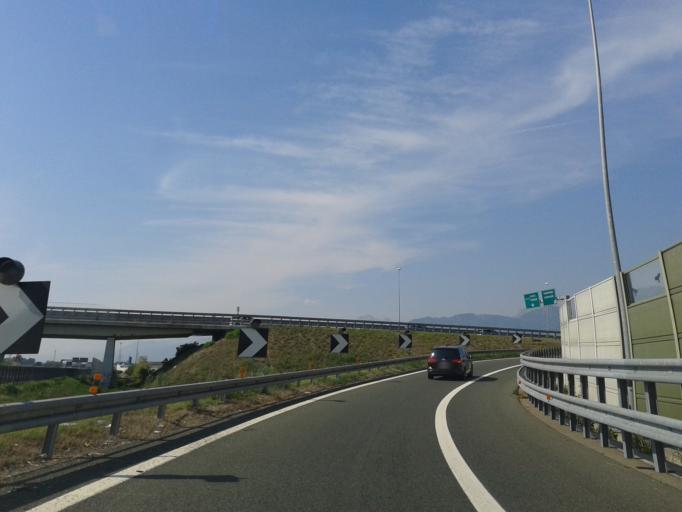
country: IT
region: Tuscany
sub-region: Provincia di Lucca
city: Viareggio
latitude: 43.8876
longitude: 10.2634
